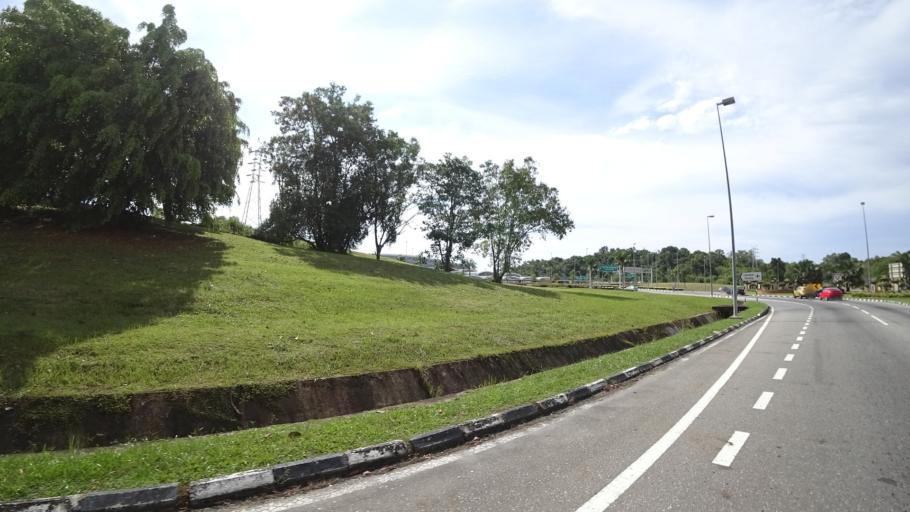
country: BN
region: Brunei and Muara
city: Bandar Seri Begawan
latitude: 4.9425
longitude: 114.9362
